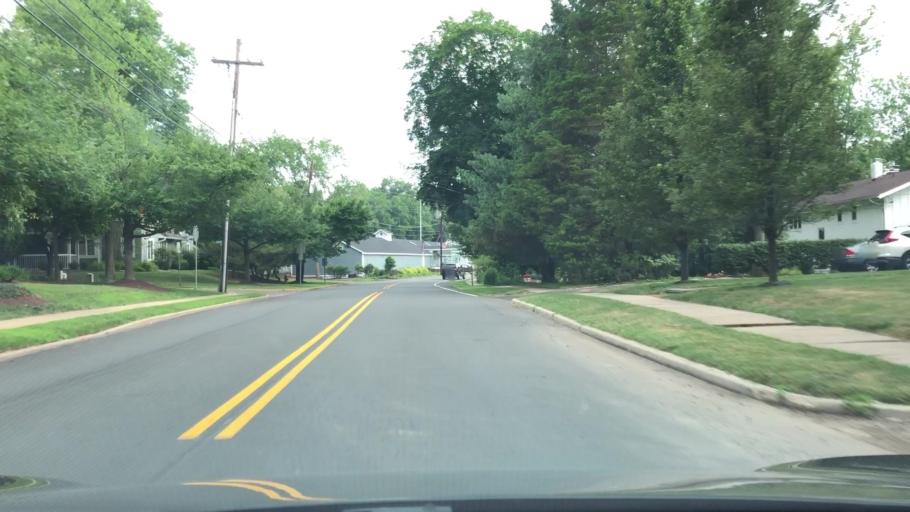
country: US
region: New Jersey
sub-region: Mercer County
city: Pennington
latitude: 40.3336
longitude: -74.7928
